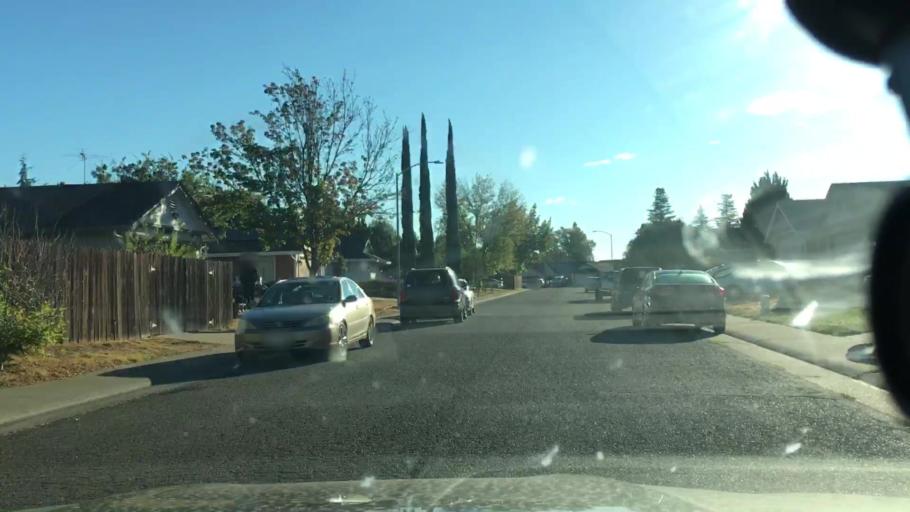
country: US
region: California
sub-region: Sacramento County
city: Antelope
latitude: 38.7041
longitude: -121.3419
